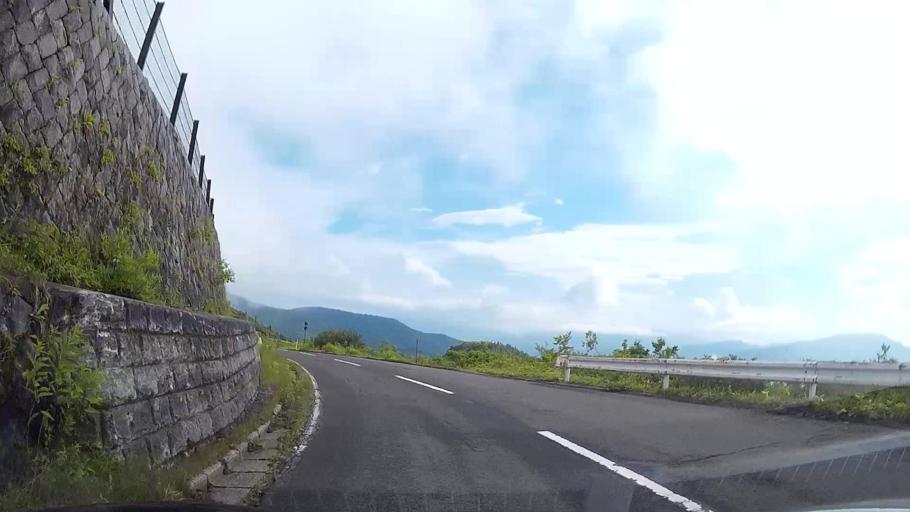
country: JP
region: Nagano
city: Nakano
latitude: 36.6457
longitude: 138.5250
